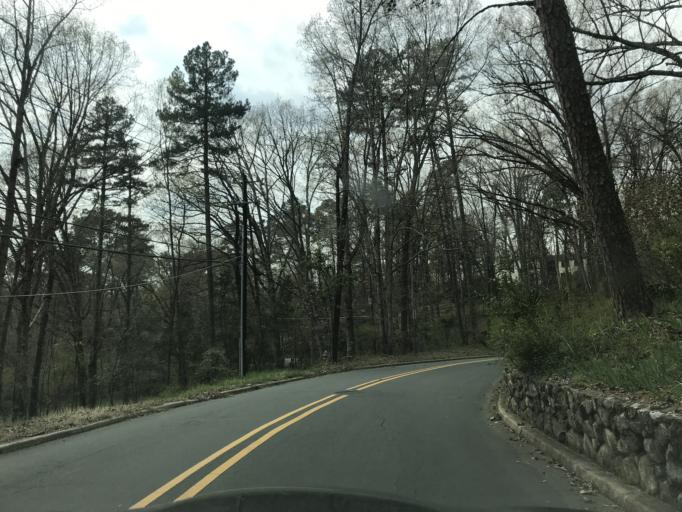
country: US
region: North Carolina
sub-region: Orange County
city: Chapel Hill
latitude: 35.9073
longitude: -79.0395
